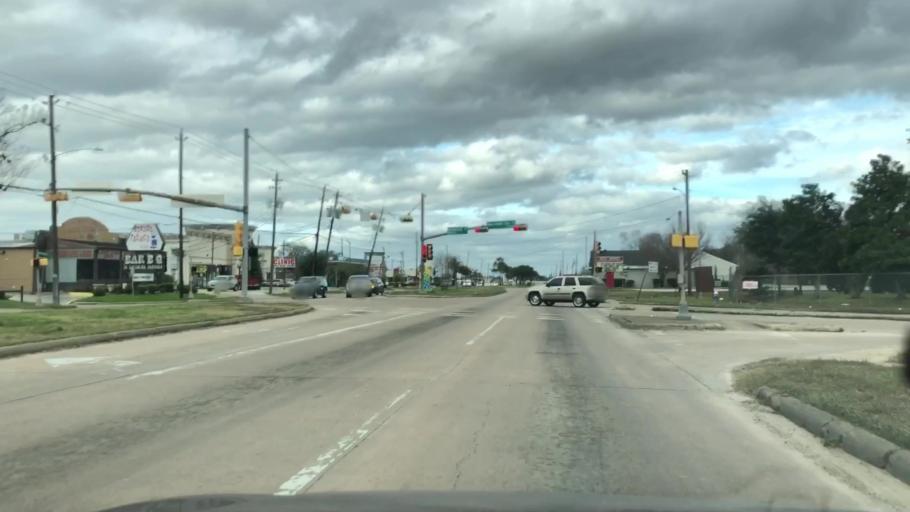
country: US
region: Texas
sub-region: Fort Bend County
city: Missouri City
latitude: 29.6146
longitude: -95.4648
